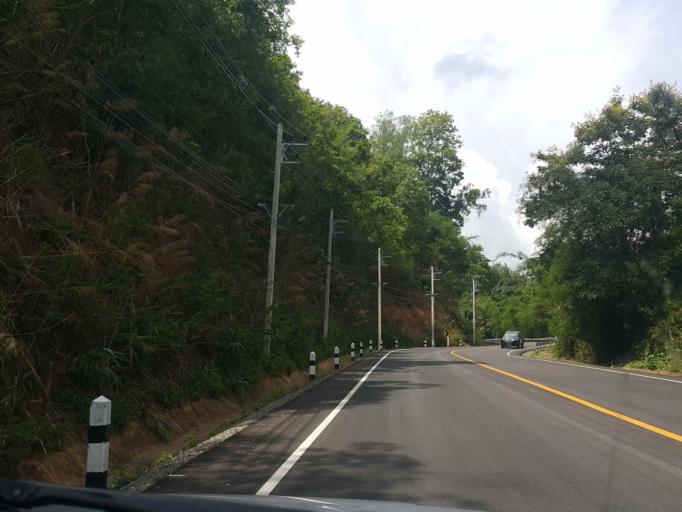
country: TH
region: Nan
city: Ban Luang
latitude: 18.8733
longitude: 100.5084
